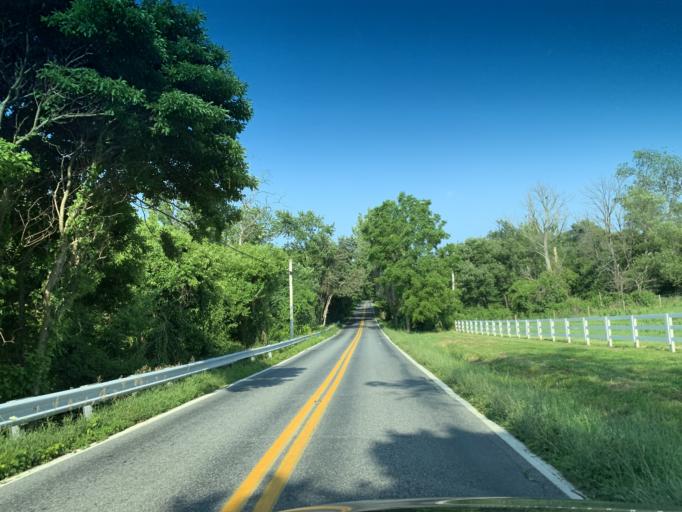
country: US
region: Maryland
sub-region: Montgomery County
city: Clarksburg
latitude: 39.2480
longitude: -77.3569
